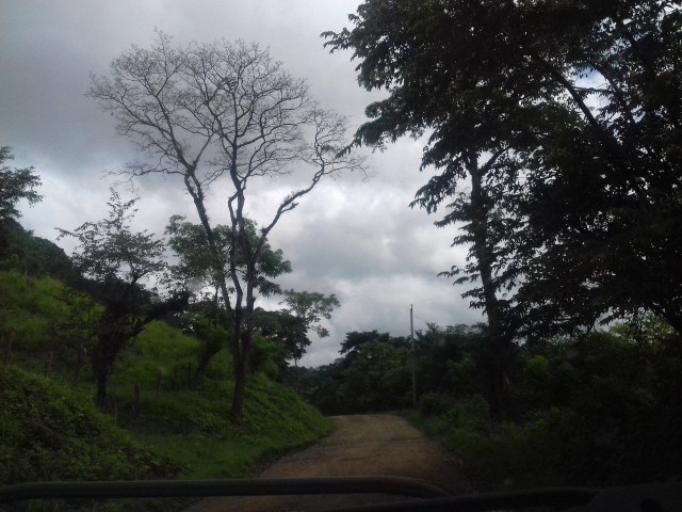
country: NI
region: Matagalpa
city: Matiguas
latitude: 12.8635
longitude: -85.3879
